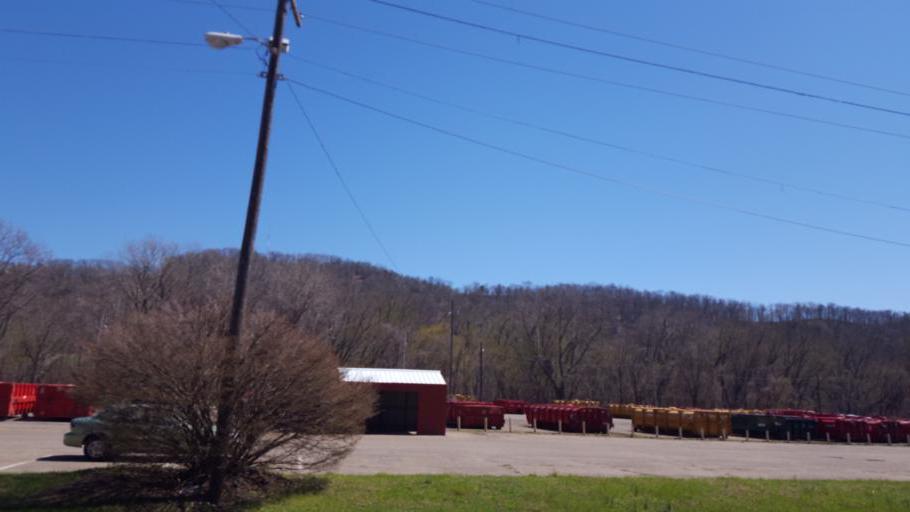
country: US
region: Ohio
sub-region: Belmont County
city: Martins Ferry
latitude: 40.1025
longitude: -80.7110
